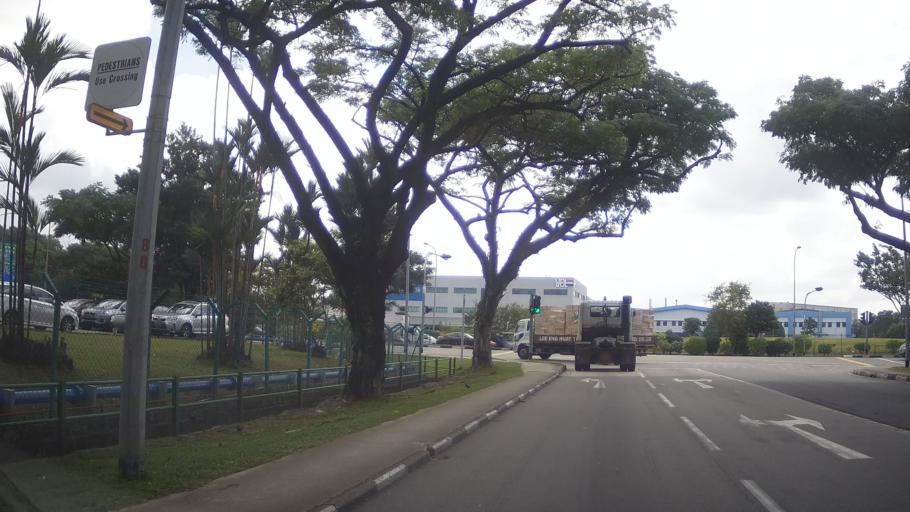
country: MY
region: Johor
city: Johor Bahru
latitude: 1.3205
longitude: 103.6784
